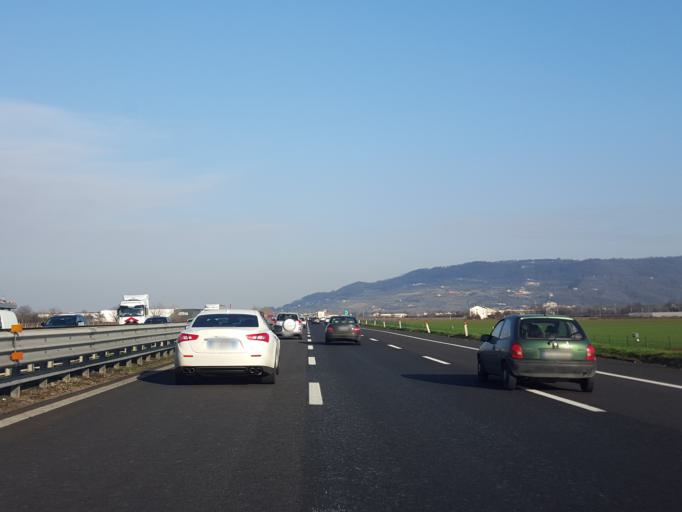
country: IT
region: Veneto
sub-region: Provincia di Vicenza
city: Montebello Vicentino
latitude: 45.4644
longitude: 11.4085
